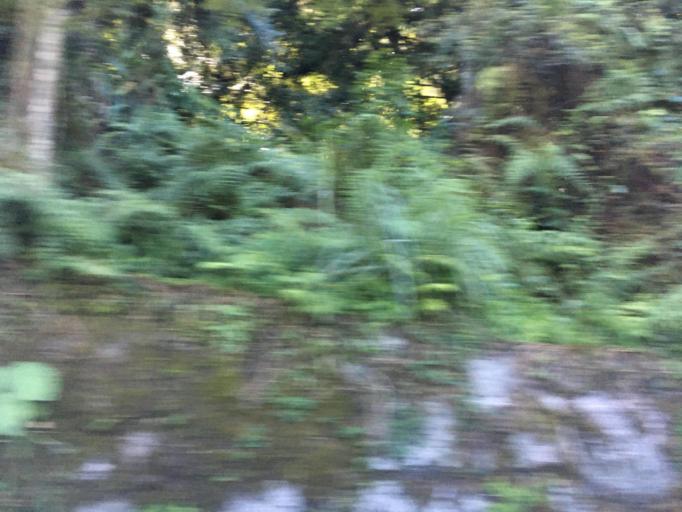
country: TW
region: Taiwan
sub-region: Yilan
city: Yilan
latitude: 24.5389
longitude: 121.5122
